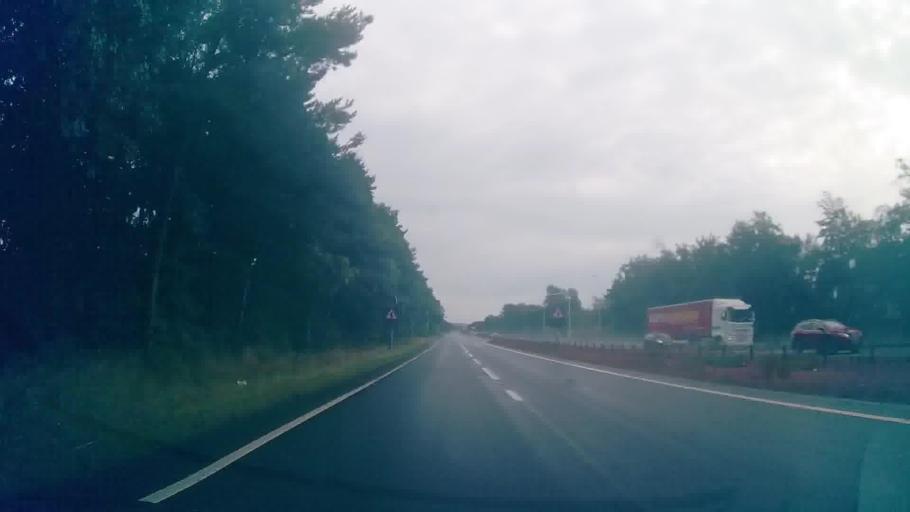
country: GB
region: Scotland
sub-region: Dumfries and Galloway
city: Locharbriggs
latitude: 55.0669
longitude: -3.5243
